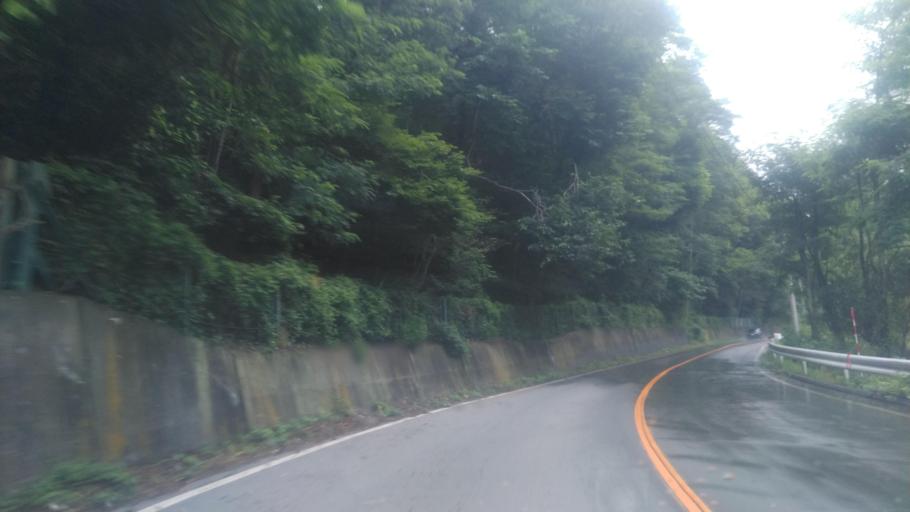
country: JP
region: Nagano
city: Ueda
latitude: 36.4911
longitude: 138.3685
